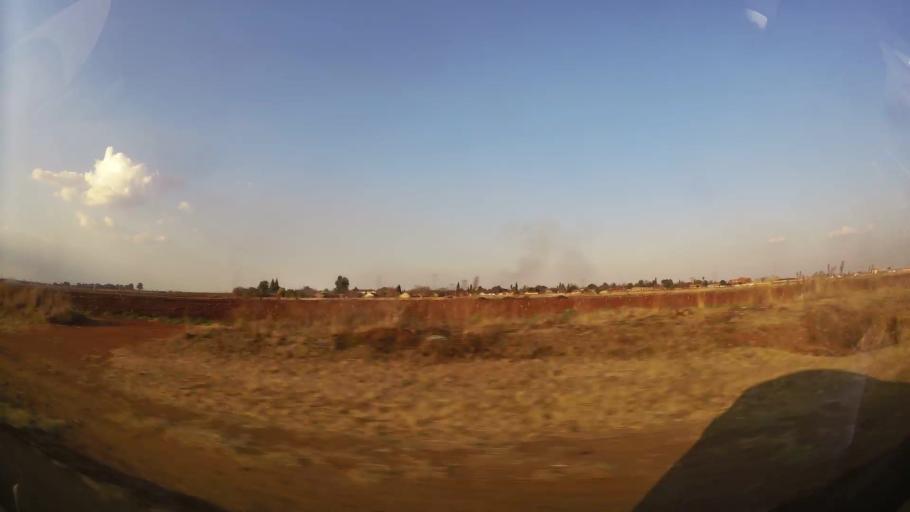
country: ZA
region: Gauteng
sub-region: Ekurhuleni Metropolitan Municipality
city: Germiston
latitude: -26.3045
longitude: 28.2325
